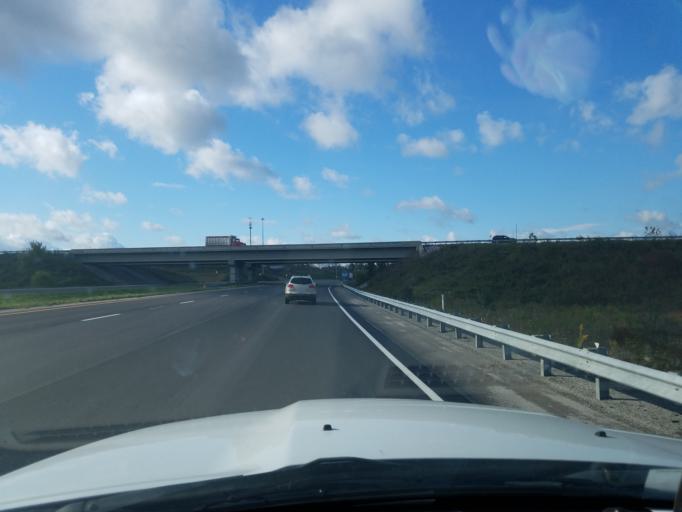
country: US
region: Kentucky
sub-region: Pulaski County
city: Somerset
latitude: 37.1056
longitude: -84.6618
